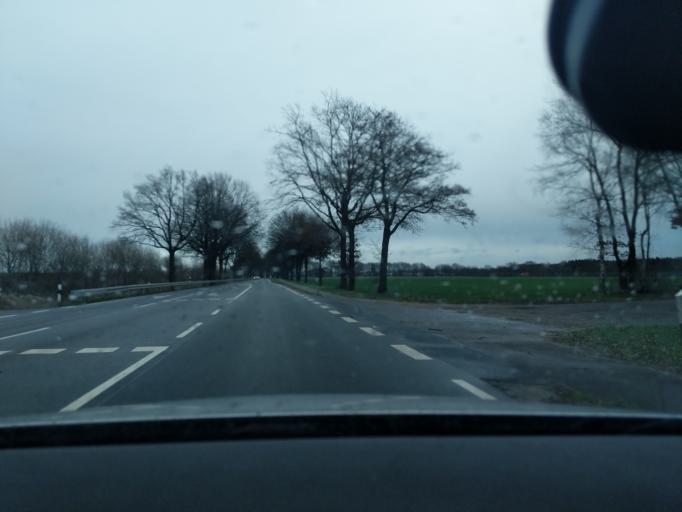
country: DE
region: Lower Saxony
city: Dudenbuttel
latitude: 53.5739
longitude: 9.3943
